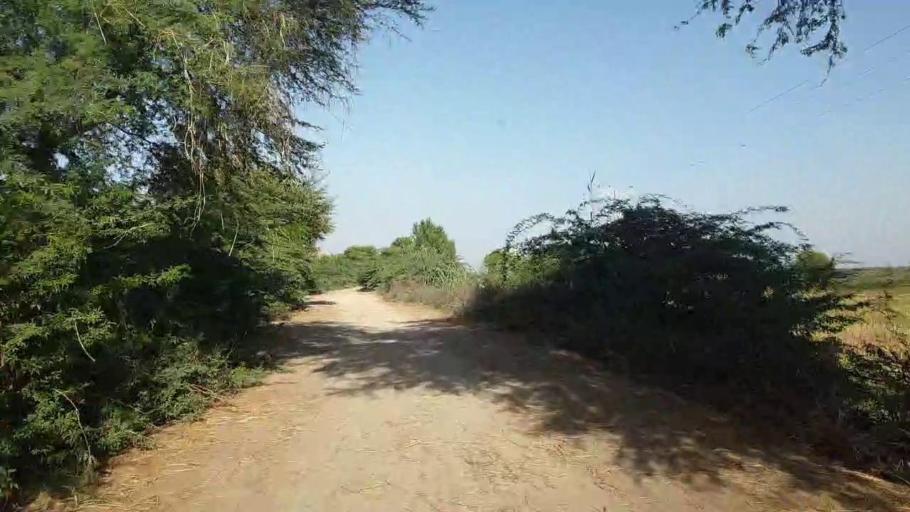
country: PK
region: Sindh
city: Badin
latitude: 24.6050
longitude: 68.9236
